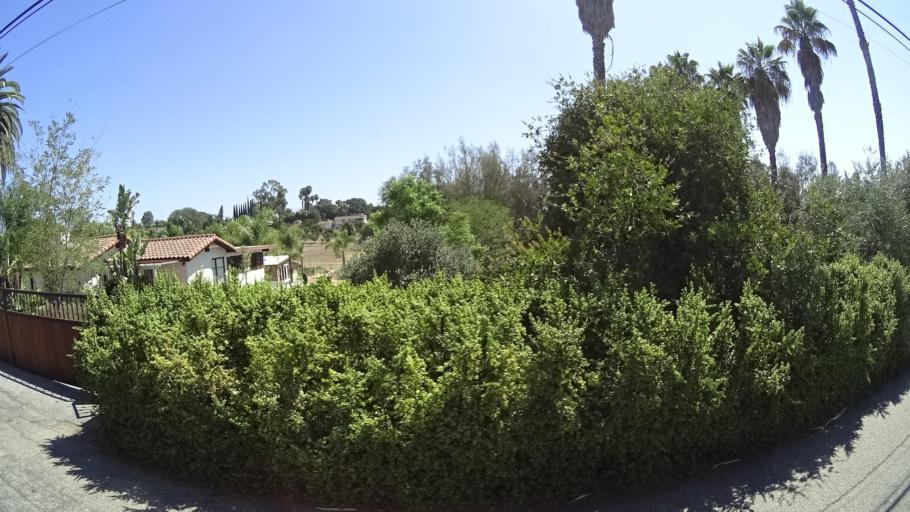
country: US
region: California
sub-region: San Diego County
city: Fallbrook
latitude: 33.3609
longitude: -117.2145
